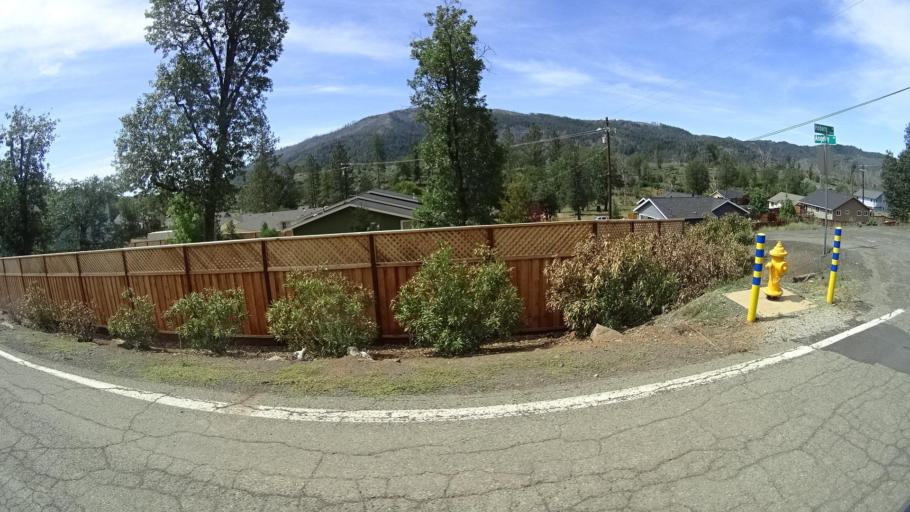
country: US
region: California
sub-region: Lake County
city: Cobb
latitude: 38.8453
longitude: -122.7336
